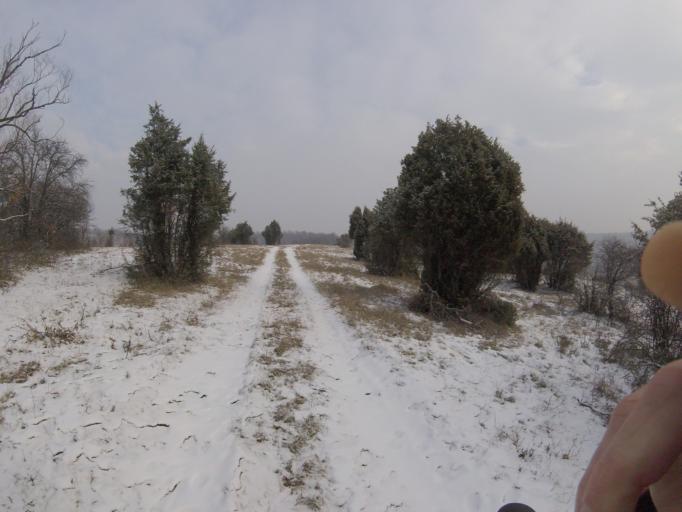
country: HU
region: Heves
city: Sirok
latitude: 47.9590
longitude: 20.2067
